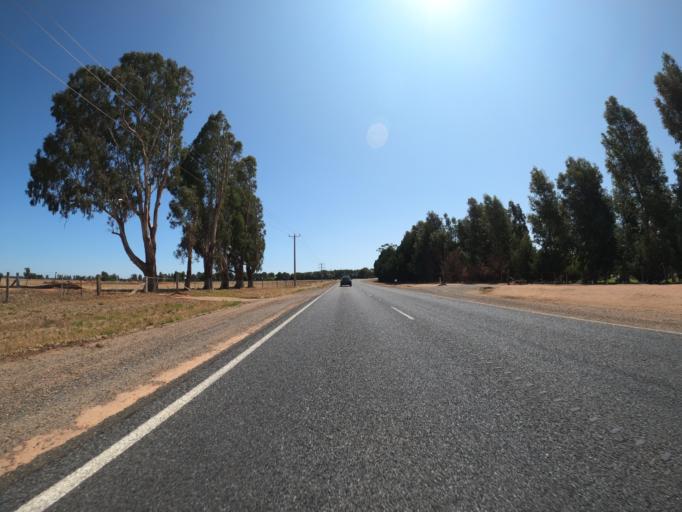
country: AU
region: Victoria
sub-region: Moira
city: Yarrawonga
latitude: -36.0276
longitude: 146.0763
